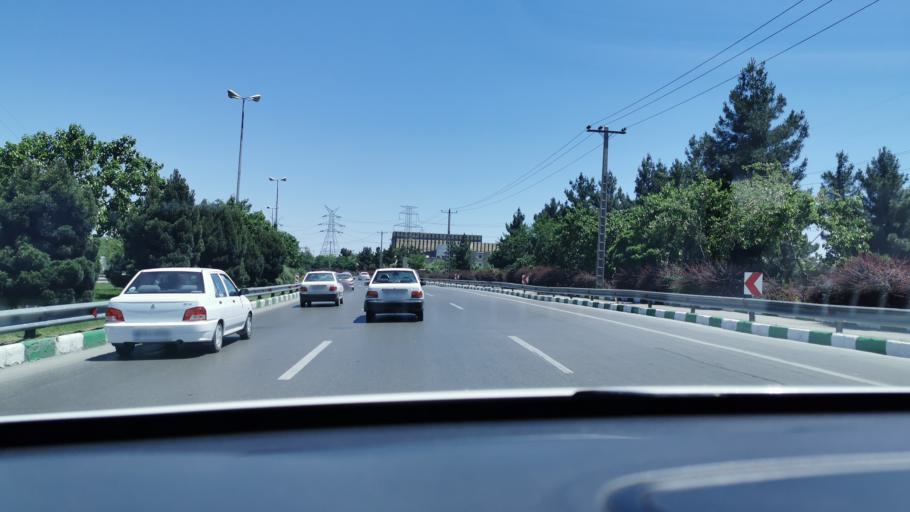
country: IR
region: Razavi Khorasan
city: Mashhad
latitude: 36.2581
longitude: 59.5885
